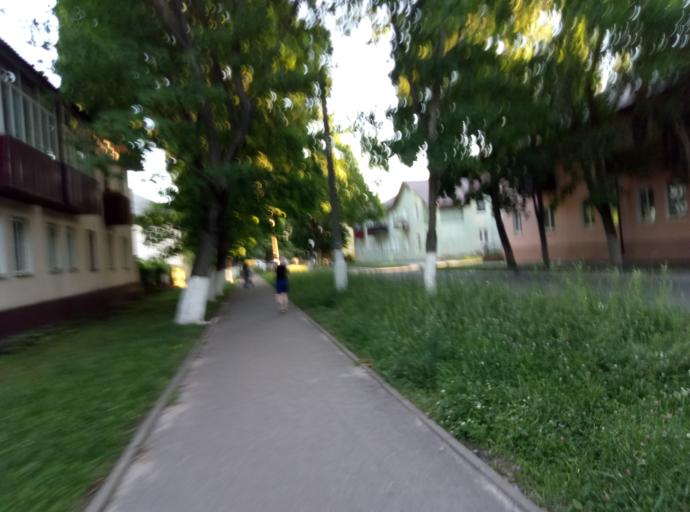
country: RU
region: Kursk
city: Kursk
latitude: 51.6734
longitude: 36.1526
